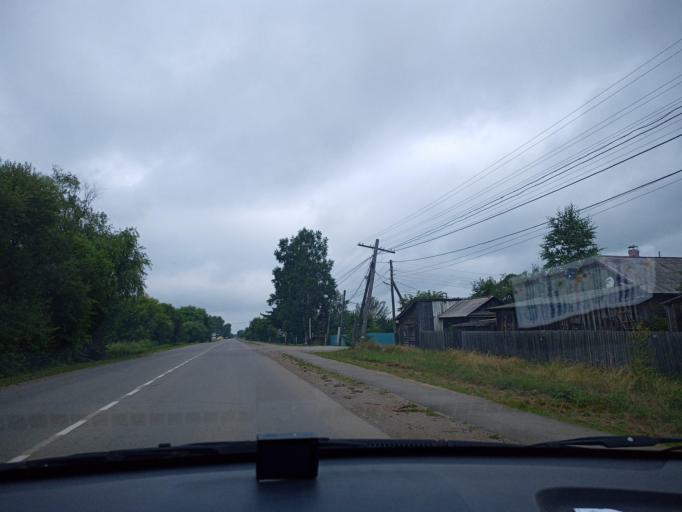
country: RU
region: Primorskiy
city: Novopokrovka
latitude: 45.8972
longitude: 134.8793
